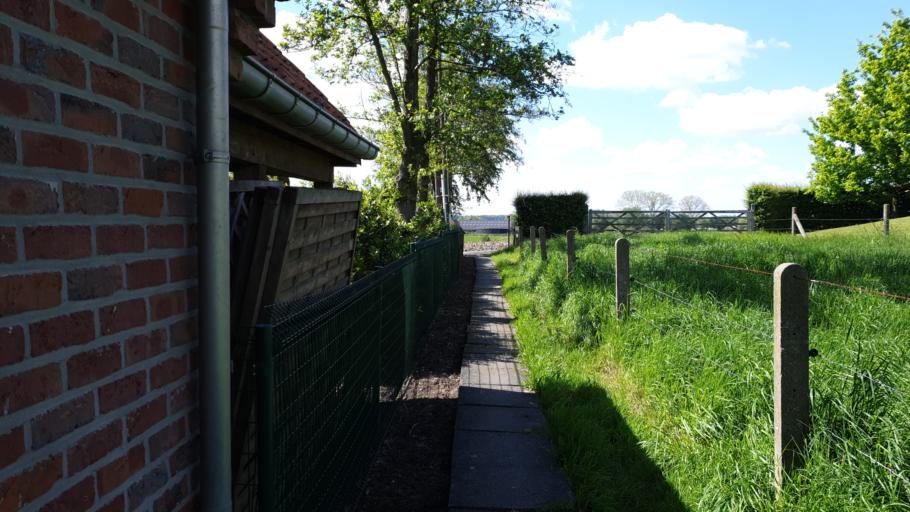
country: BE
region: Flanders
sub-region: Provincie West-Vlaanderen
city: Zwevegem
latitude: 50.8204
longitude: 3.3675
